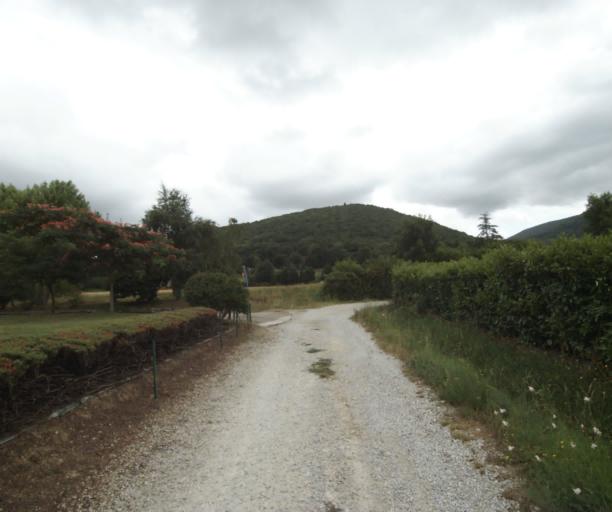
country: FR
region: Midi-Pyrenees
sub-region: Departement du Tarn
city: Soreze
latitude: 43.4475
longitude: 2.0606
